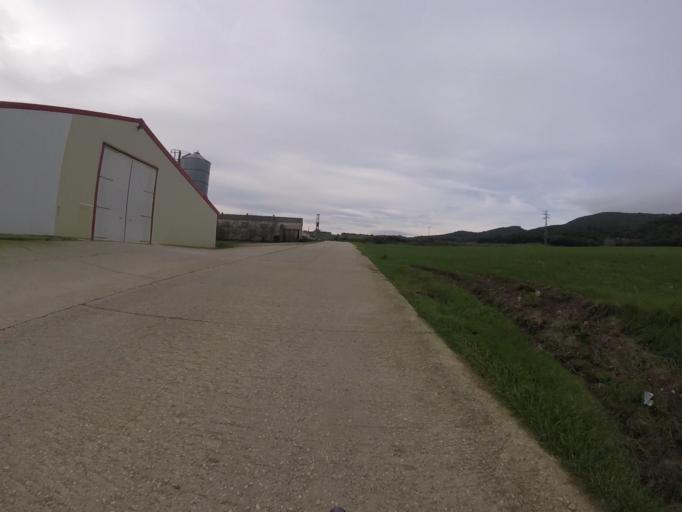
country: ES
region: Navarre
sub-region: Provincia de Navarra
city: Estella
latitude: 42.7215
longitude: -2.0299
